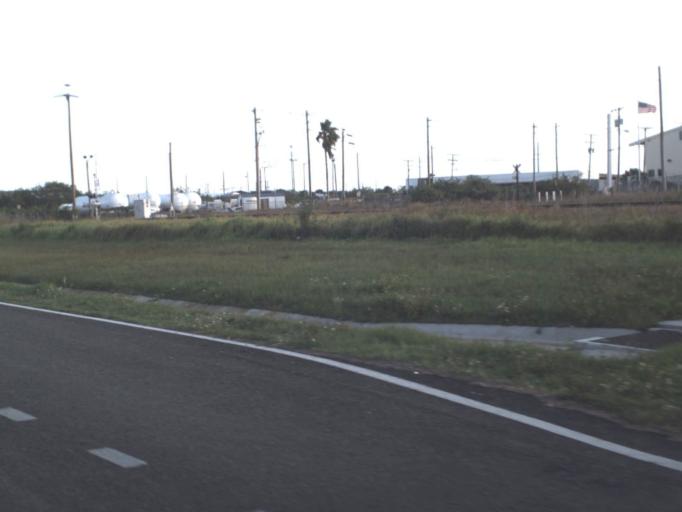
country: US
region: Florida
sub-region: Brevard County
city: Rockledge
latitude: 28.2746
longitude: -80.6930
